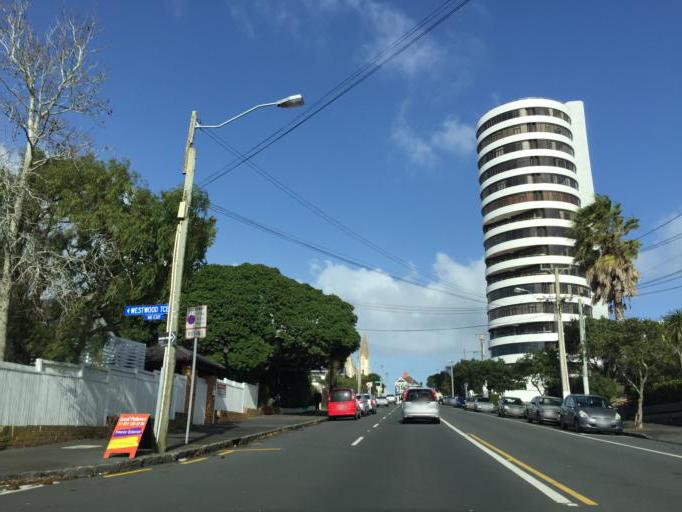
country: NZ
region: Auckland
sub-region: Auckland
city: Auckland
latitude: -36.8438
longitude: 174.7420
